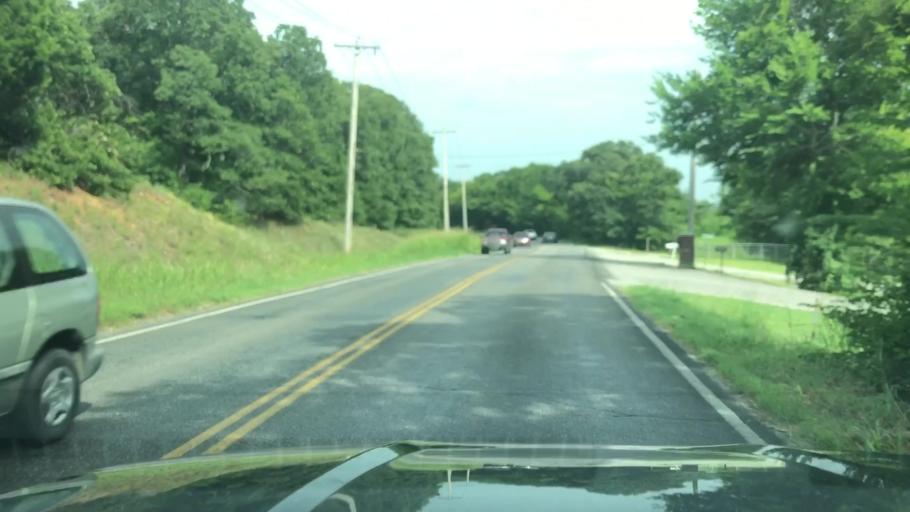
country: US
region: Oklahoma
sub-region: Tulsa County
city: Oakhurst
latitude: 36.0903
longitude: -96.0788
